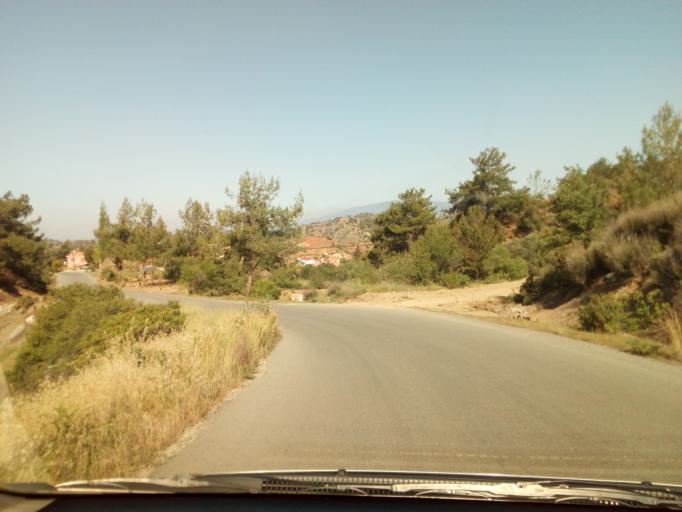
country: CY
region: Limassol
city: Pelendri
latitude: 34.8312
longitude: 33.0413
